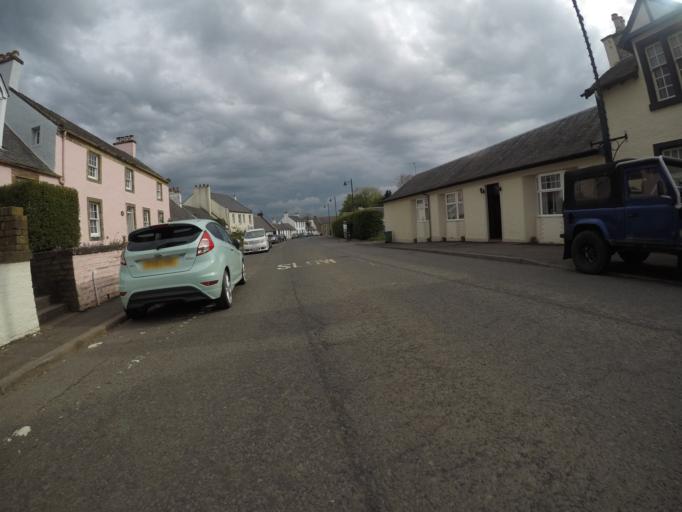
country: GB
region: Scotland
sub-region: East Ayrshire
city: Kilmarnock
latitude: 55.6554
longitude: -4.4456
